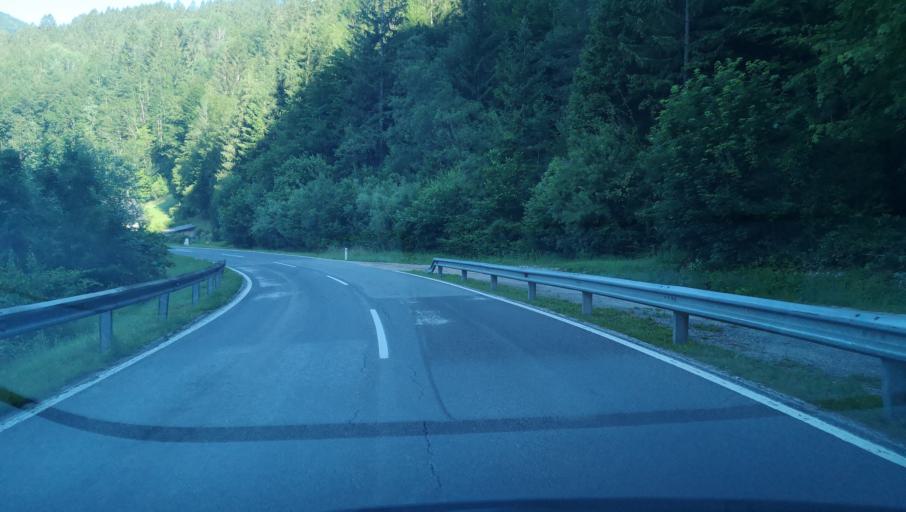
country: AT
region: Lower Austria
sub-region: Politischer Bezirk Amstetten
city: Opponitz
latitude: 47.8837
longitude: 14.8174
